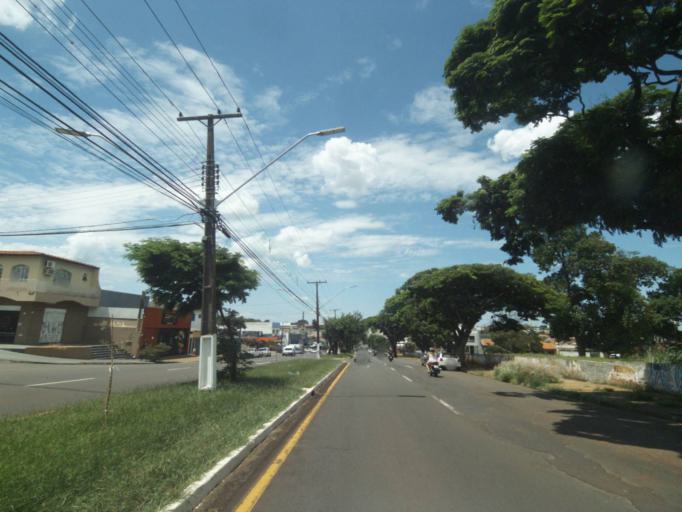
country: BR
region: Parana
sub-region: Londrina
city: Londrina
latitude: -23.3049
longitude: -51.1983
